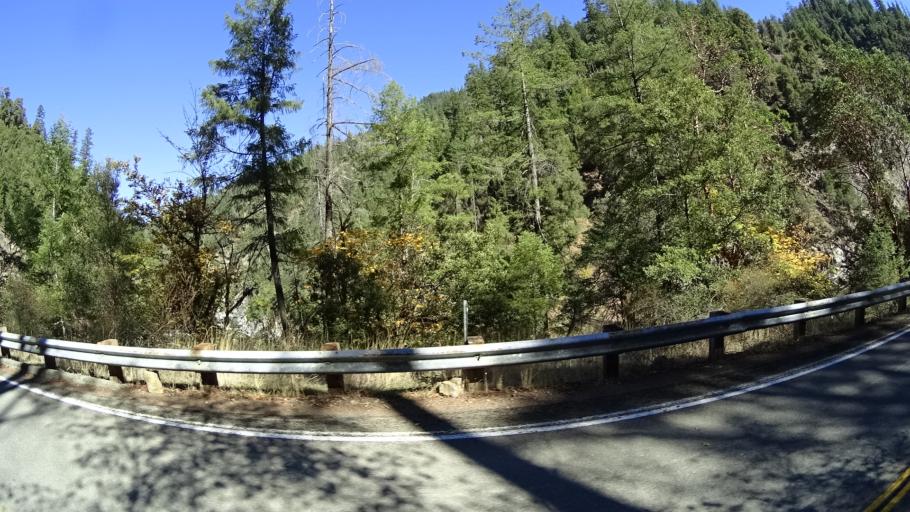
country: US
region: California
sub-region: Siskiyou County
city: Happy Camp
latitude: 41.3513
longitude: -123.4093
